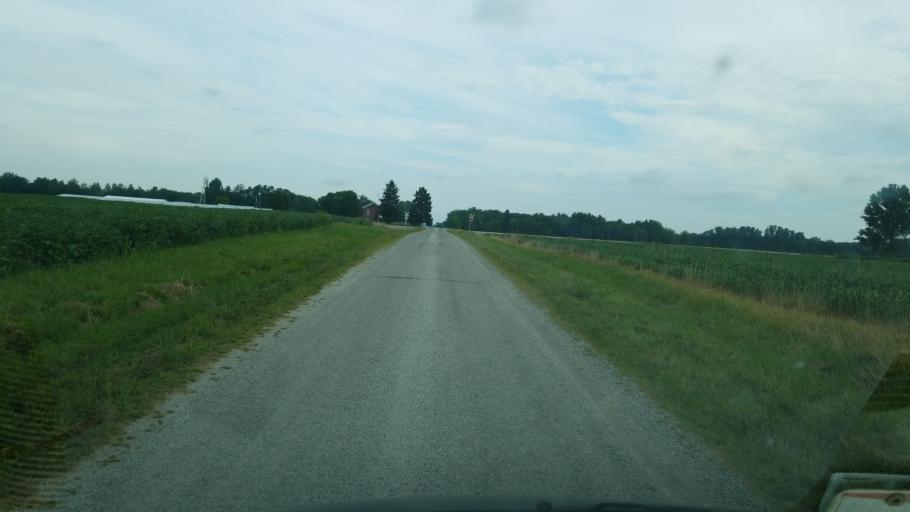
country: US
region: Ohio
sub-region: Crawford County
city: Bucyrus
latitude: 40.9564
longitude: -83.0550
